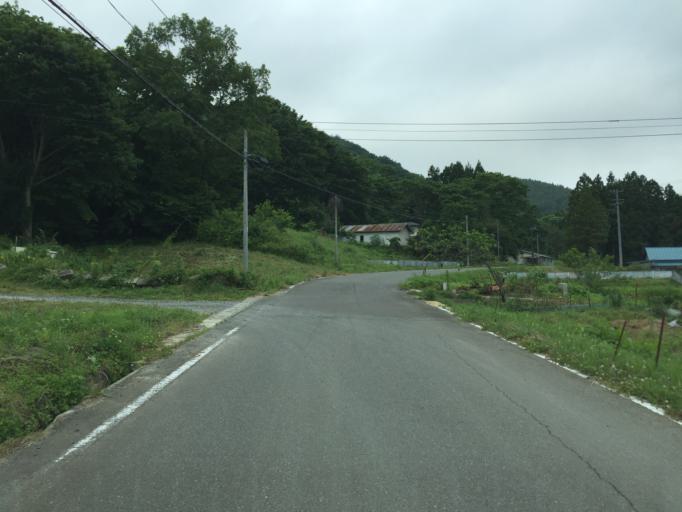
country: JP
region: Fukushima
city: Yanagawamachi-saiwaicho
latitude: 37.7886
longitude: 140.7127
